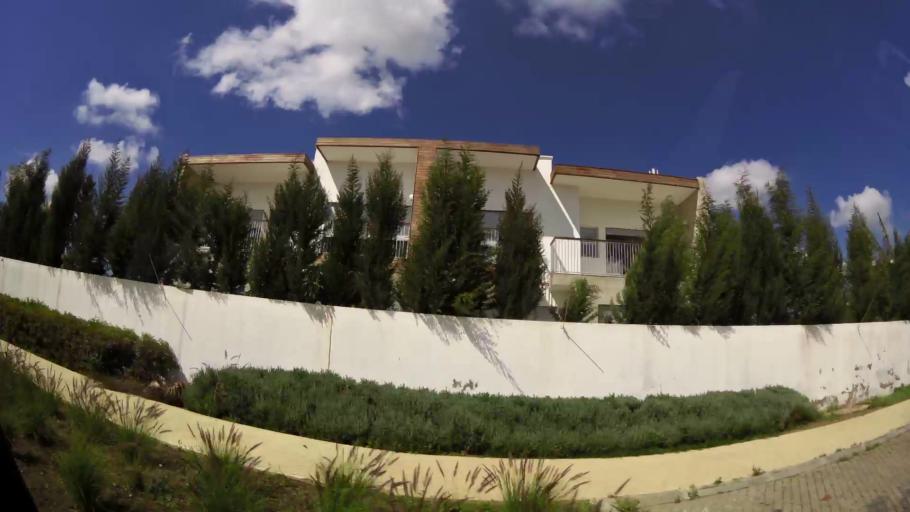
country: MA
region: Grand Casablanca
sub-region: Nouaceur
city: Bouskoura
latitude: 33.4913
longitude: -7.5875
